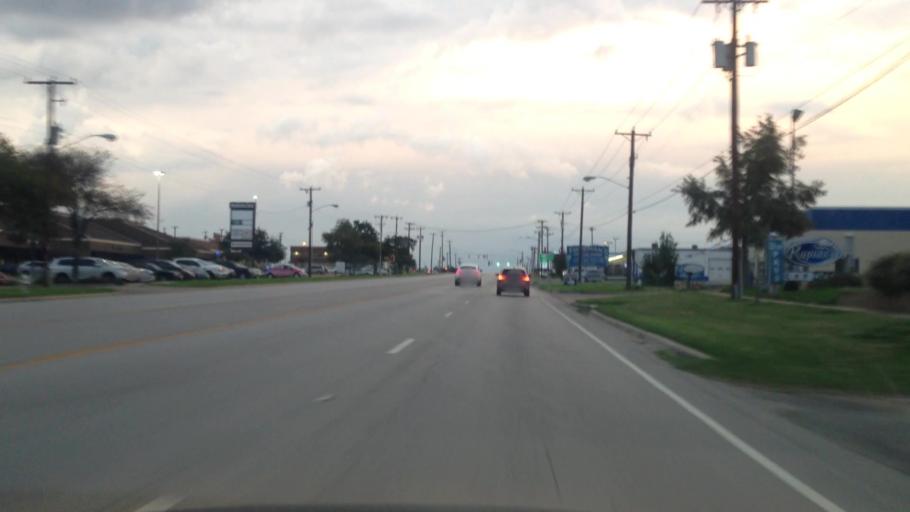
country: US
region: Texas
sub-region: Tarrant County
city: Colleyville
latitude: 32.8651
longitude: -97.1746
